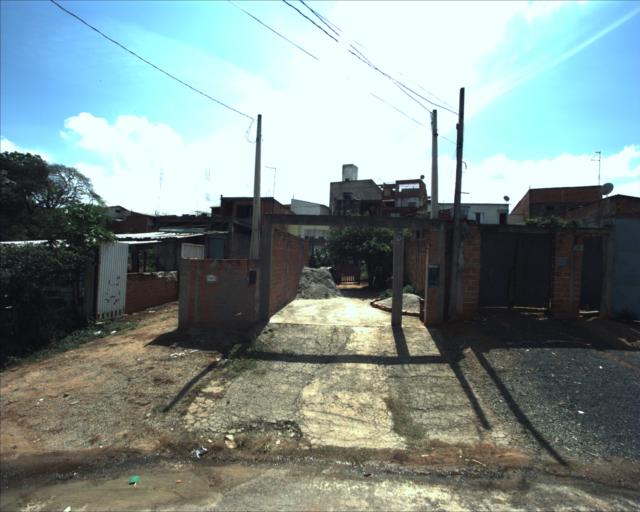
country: BR
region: Sao Paulo
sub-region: Sorocaba
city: Sorocaba
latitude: -23.4149
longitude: -47.4095
